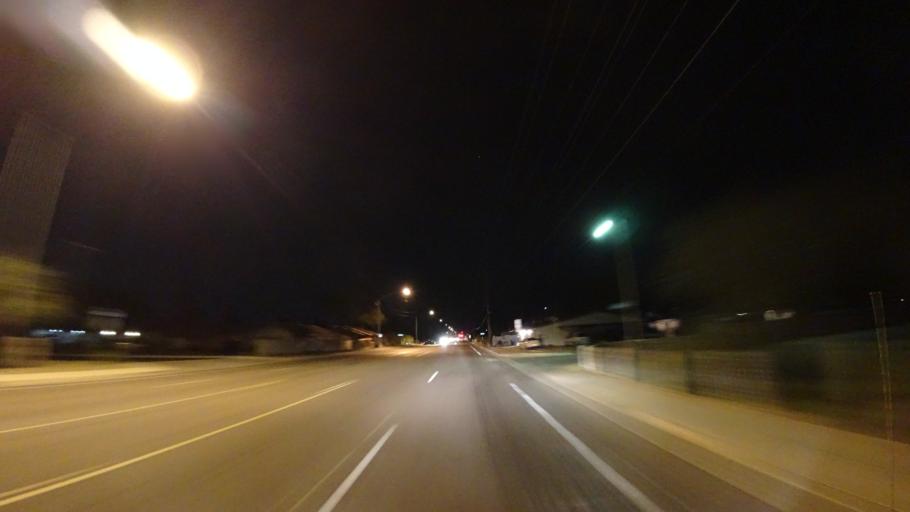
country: US
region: Arizona
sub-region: Maricopa County
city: Mesa
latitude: 33.4461
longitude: -111.8311
